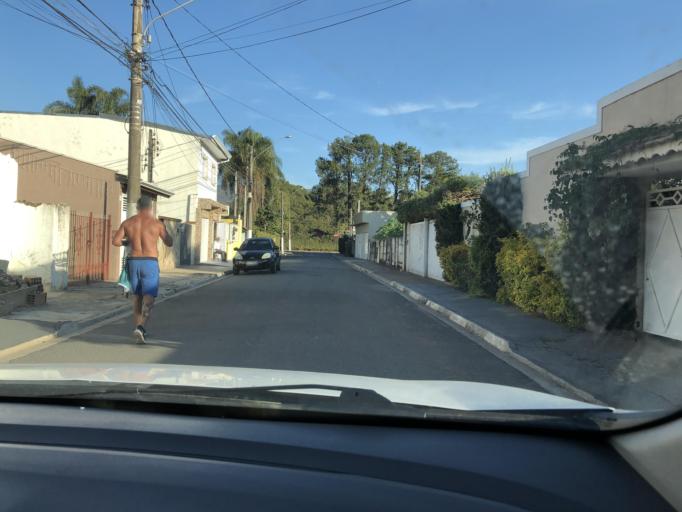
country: BR
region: Sao Paulo
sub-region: Atibaia
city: Atibaia
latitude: -23.1073
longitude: -46.5300
